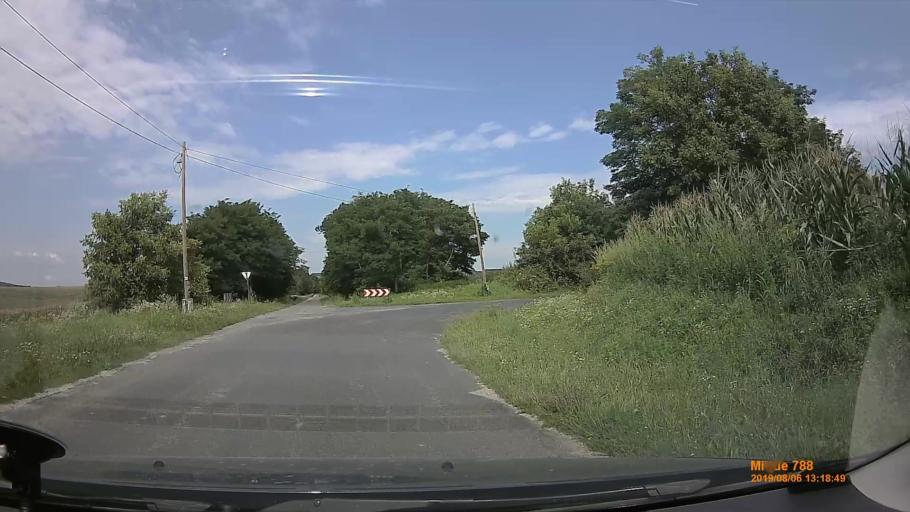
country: HU
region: Zala
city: Pacsa
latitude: 46.6354
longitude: 17.0616
